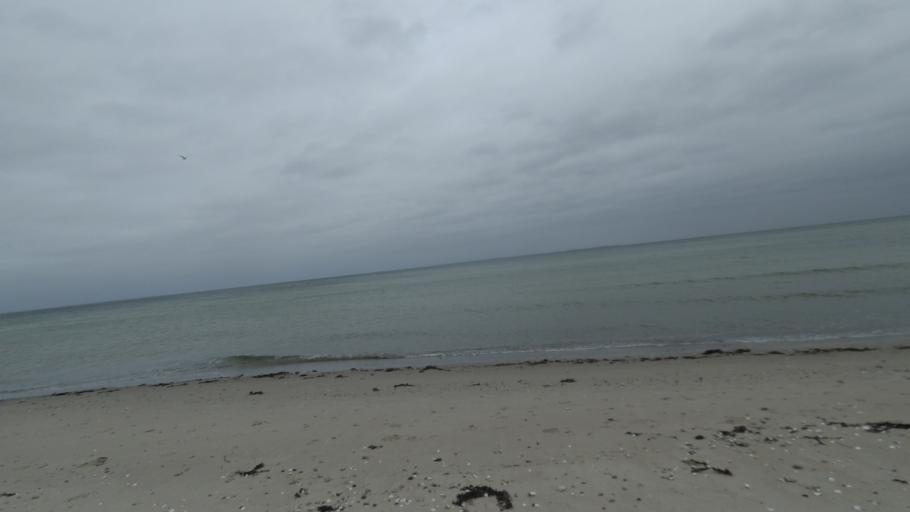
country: DK
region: Central Jutland
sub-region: Arhus Kommune
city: Malling
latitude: 55.9814
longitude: 10.2526
